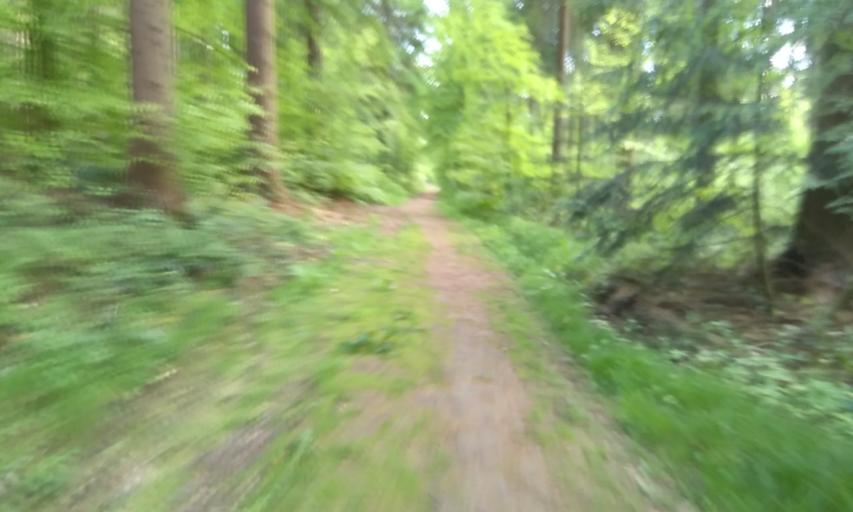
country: DE
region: Lower Saxony
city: Buxtehude
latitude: 53.4719
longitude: 9.6497
